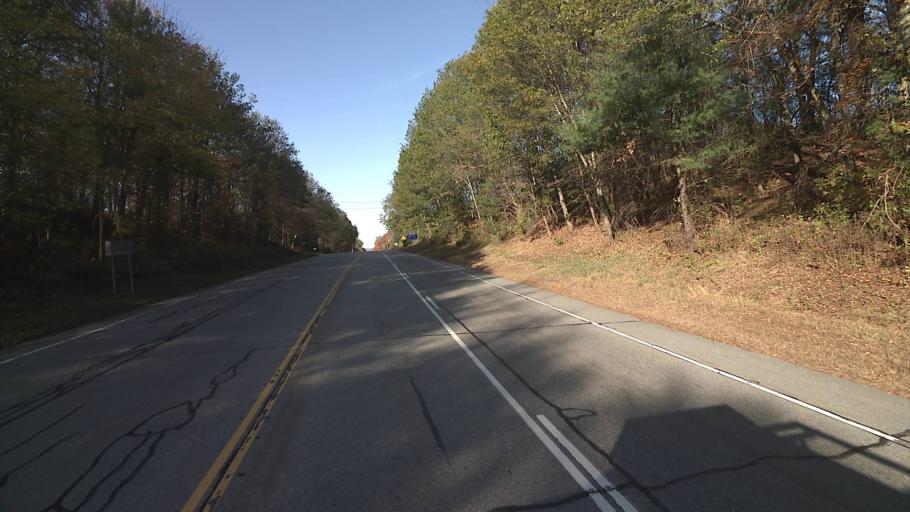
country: US
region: Connecticut
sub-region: Windham County
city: Killingly Center
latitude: 41.7908
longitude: -71.8123
